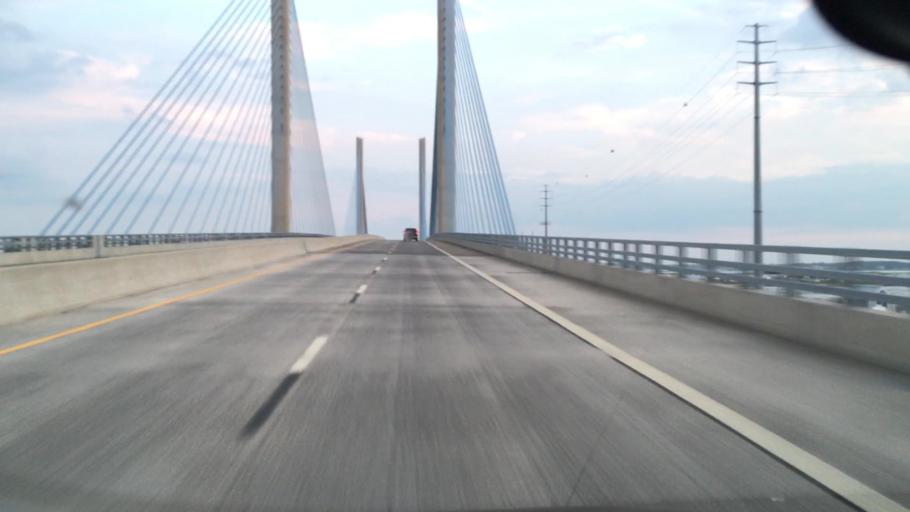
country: US
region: Delaware
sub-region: Sussex County
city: Ocean View
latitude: 38.6108
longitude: -75.0642
